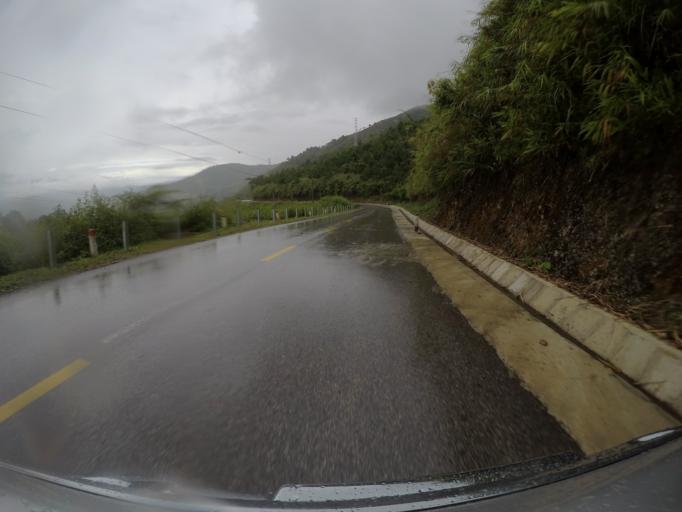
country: VN
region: Lai Chau
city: Than Uyen
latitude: 22.1192
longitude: 103.8163
